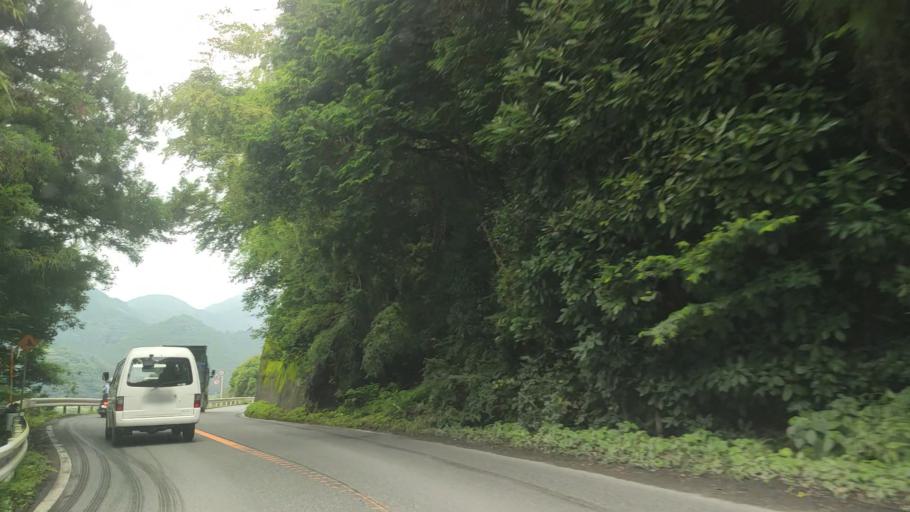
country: JP
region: Shizuoka
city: Fujinomiya
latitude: 35.2240
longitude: 138.5410
